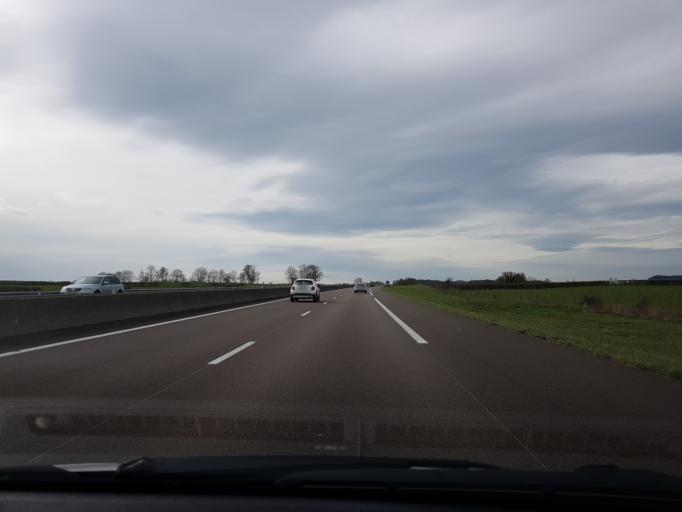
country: FR
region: Bourgogne
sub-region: Departement de la Cote-d'Or
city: Pouilly-en-Auxois
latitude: 47.2123
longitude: 4.6105
